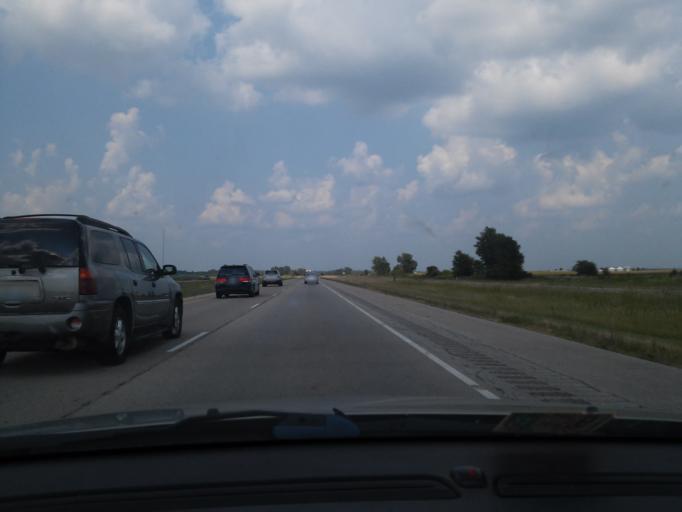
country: US
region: Illinois
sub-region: McLean County
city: Lexington
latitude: 40.6141
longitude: -88.8258
